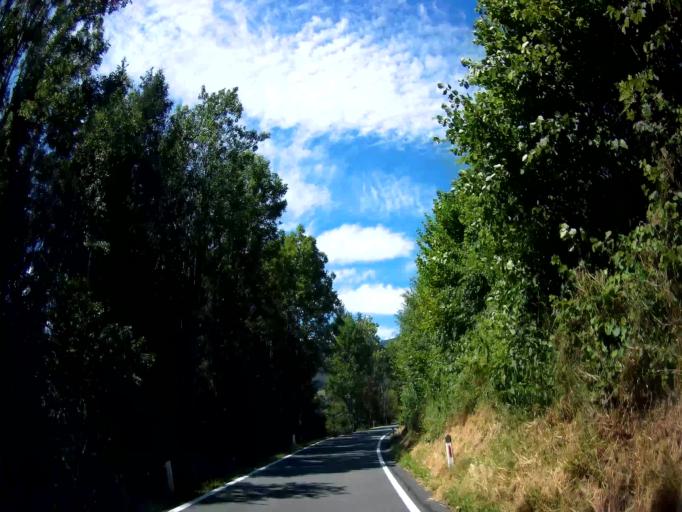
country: AT
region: Carinthia
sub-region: Politischer Bezirk Sankt Veit an der Glan
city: Glodnitz
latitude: 46.9110
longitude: 14.0925
